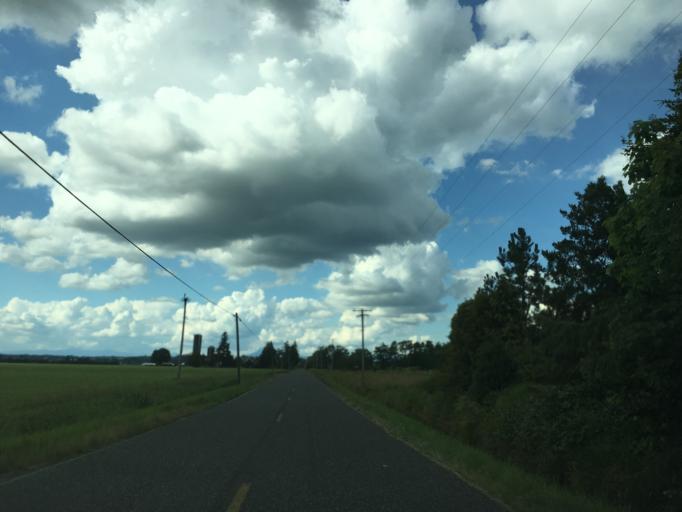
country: US
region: Washington
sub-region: Whatcom County
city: Lynden
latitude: 48.9732
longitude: -122.4738
